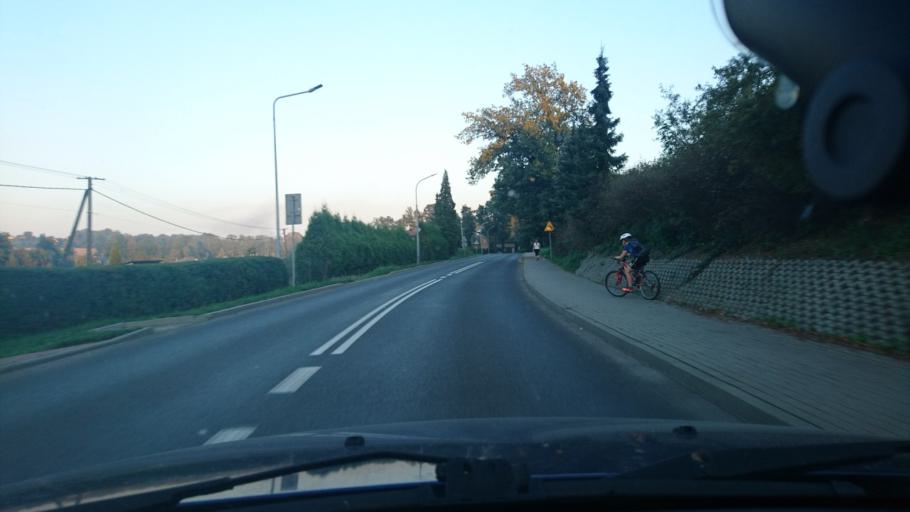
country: PL
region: Silesian Voivodeship
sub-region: Powiat bielski
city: Bestwina
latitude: 49.8970
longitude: 19.0622
